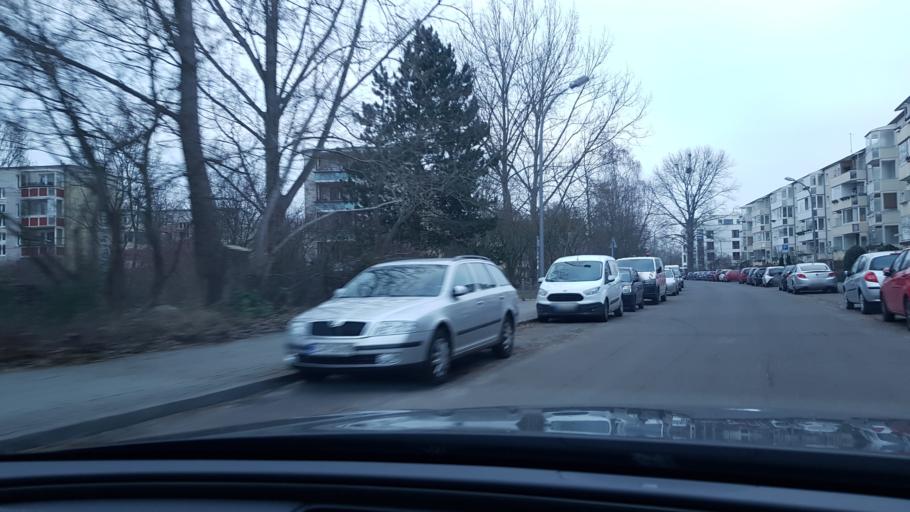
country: DE
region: Berlin
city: Grunau
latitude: 52.4267
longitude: 13.5929
